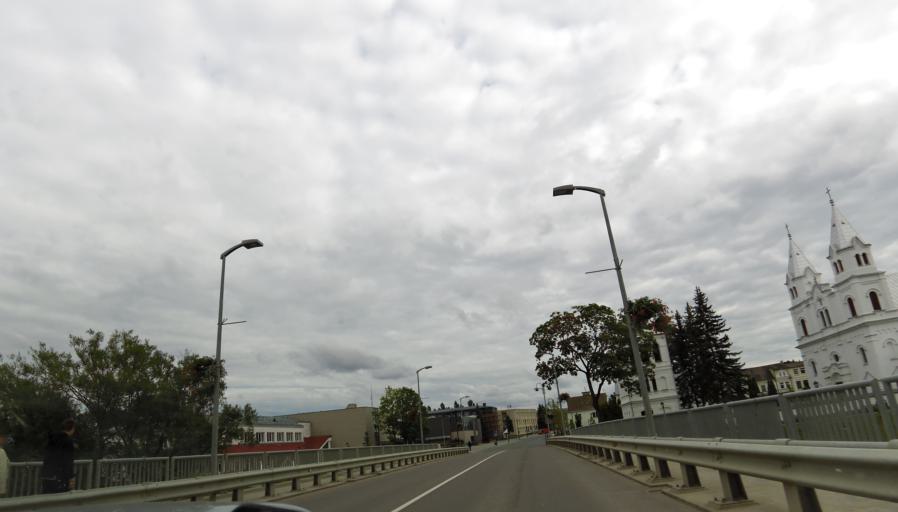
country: LT
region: Panevezys
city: Pasvalys
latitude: 56.0625
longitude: 24.3975
